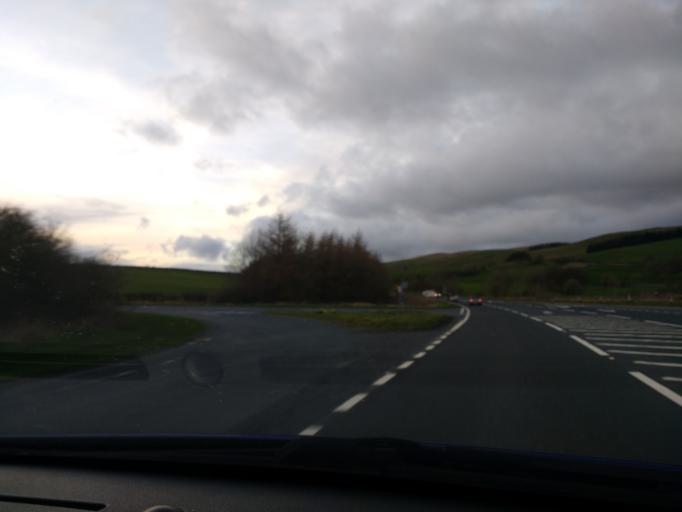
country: GB
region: England
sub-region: North Yorkshire
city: Ingleton
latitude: 54.1190
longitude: -2.3978
